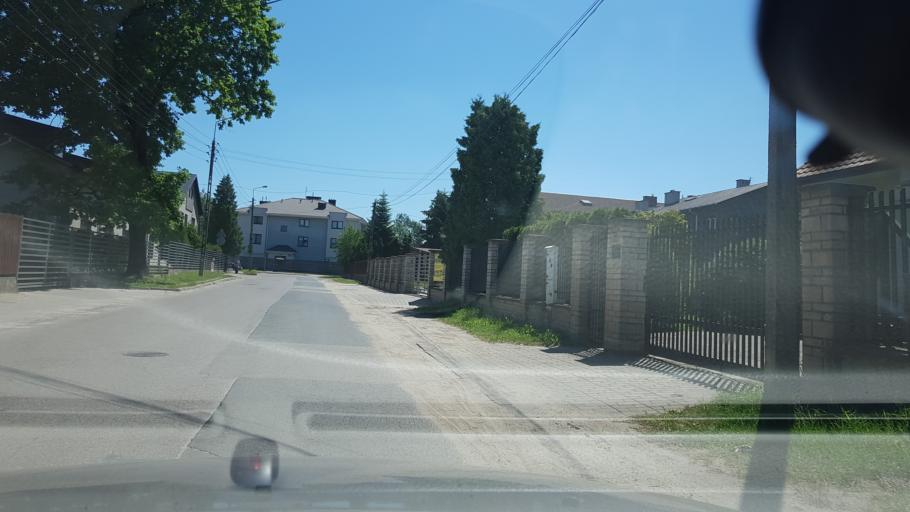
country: PL
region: Masovian Voivodeship
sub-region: Powiat wolominski
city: Marki
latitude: 52.3117
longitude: 21.1075
